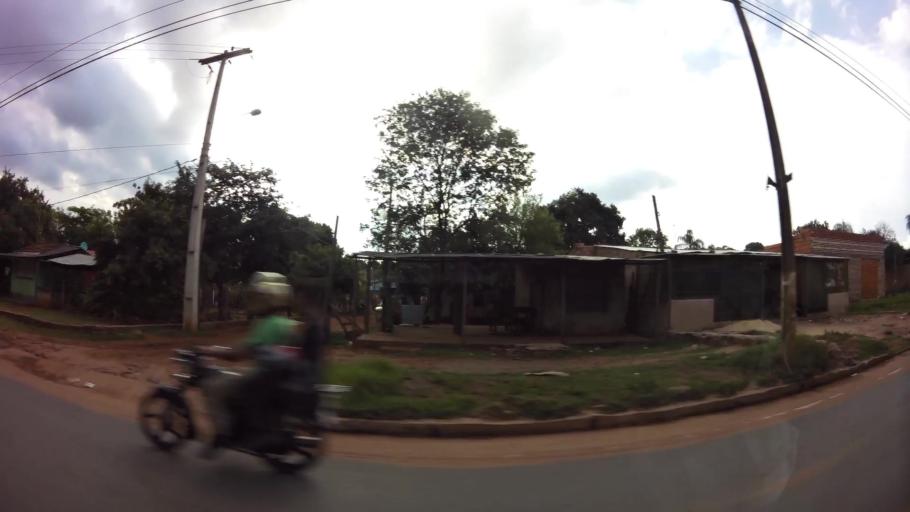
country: PY
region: Central
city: Nemby
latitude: -25.3700
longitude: -57.5423
